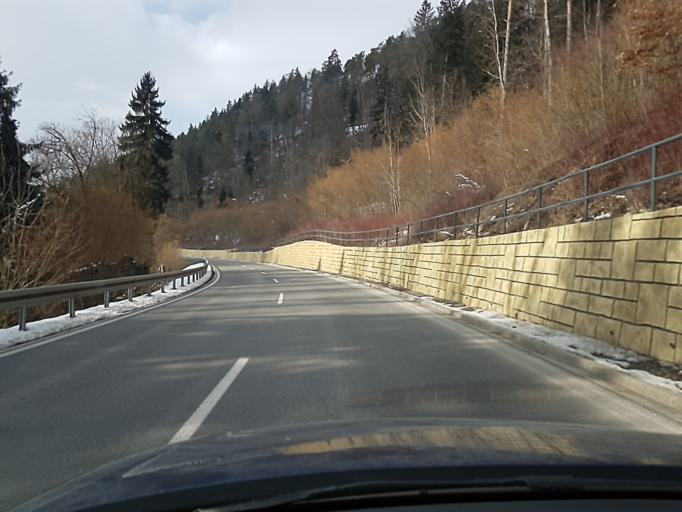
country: DE
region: Baden-Wuerttemberg
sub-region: Freiburg Region
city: Muhlheim am Bach
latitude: 48.3980
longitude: 8.6637
